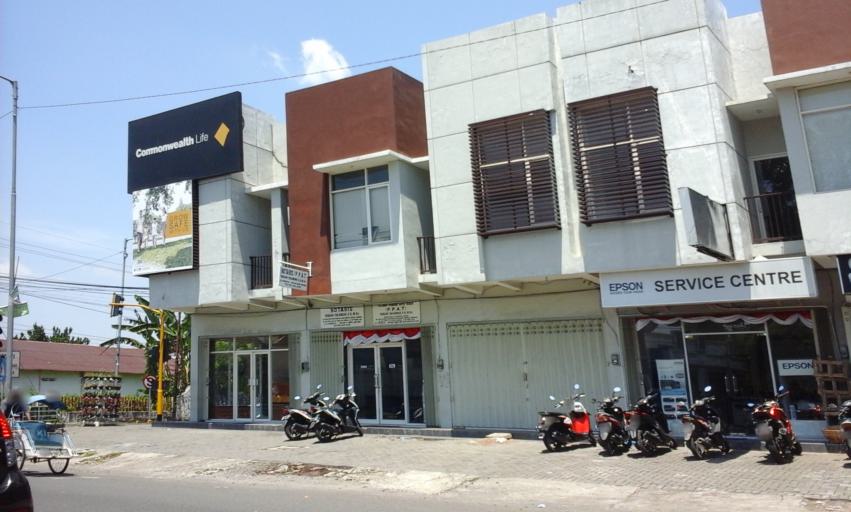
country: ID
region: East Java
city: Krajan
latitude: -8.1614
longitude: 113.7082
